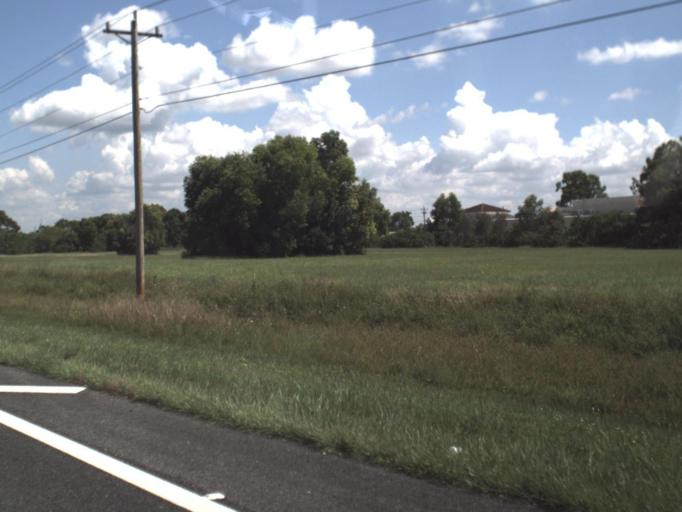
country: US
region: Florida
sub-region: Lee County
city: Lochmoor Waterway Estates
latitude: 26.6586
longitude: -81.9599
